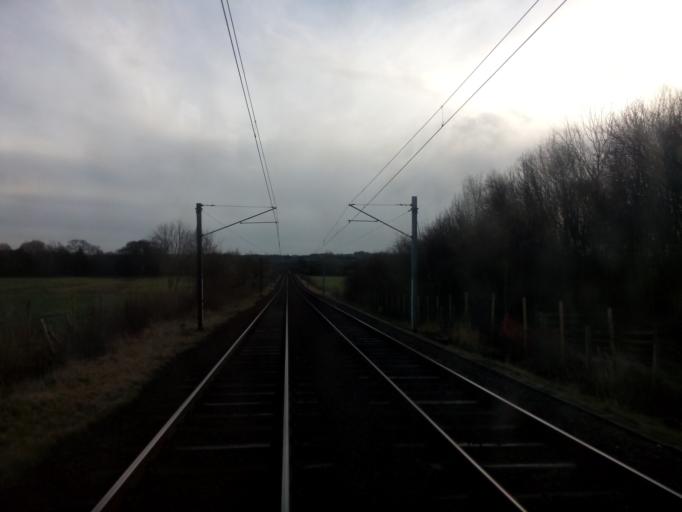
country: GB
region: England
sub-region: Newcastle upon Tyne
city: Dinnington
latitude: 55.0261
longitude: -1.7017
